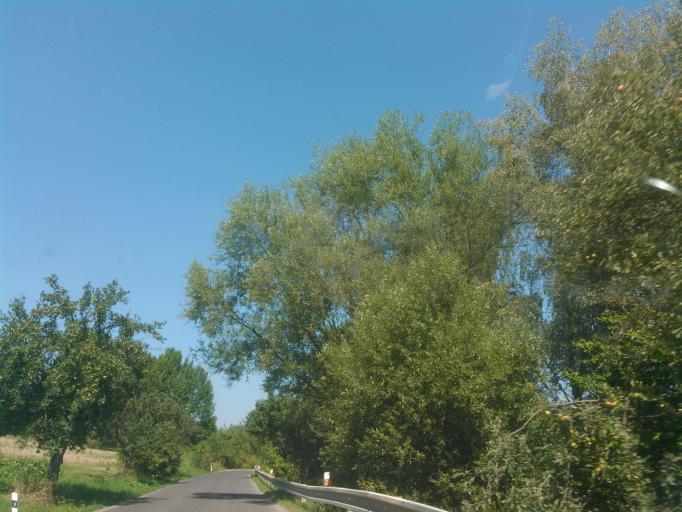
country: SK
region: Zilinsky
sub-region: Okres Liptovsky Mikulas
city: Liptovsky Mikulas
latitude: 49.0571
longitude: 19.4762
